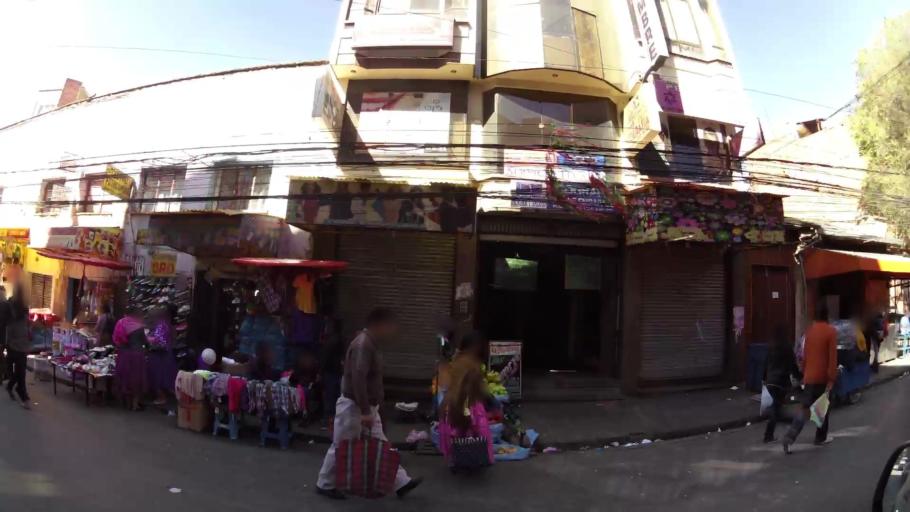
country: BO
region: La Paz
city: La Paz
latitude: -16.4957
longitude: -68.1442
